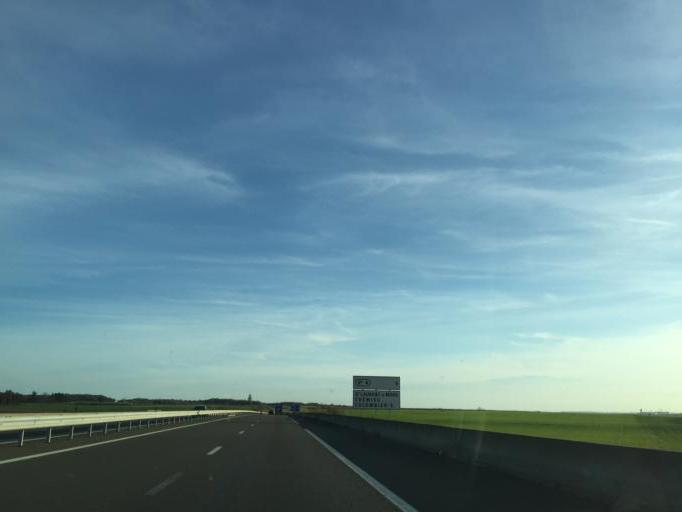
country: FR
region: Rhone-Alpes
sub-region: Departement du Rhone
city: Pusignan
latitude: 45.7600
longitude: 5.0889
